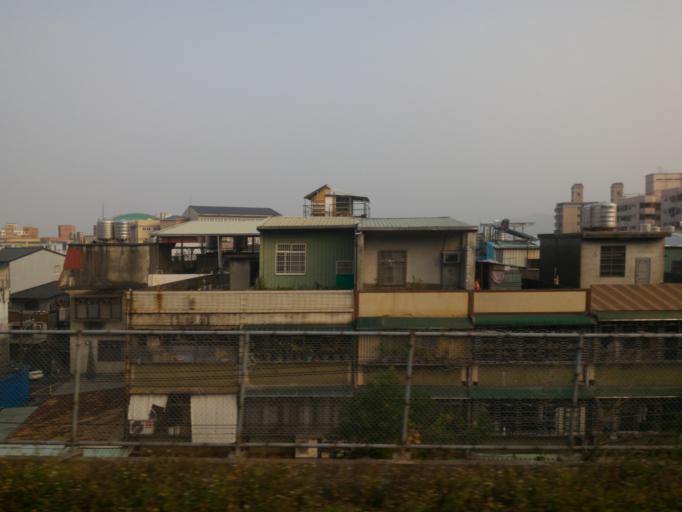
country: TW
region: Taiwan
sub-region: Taoyuan
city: Taoyuan
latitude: 24.9560
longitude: 121.3371
